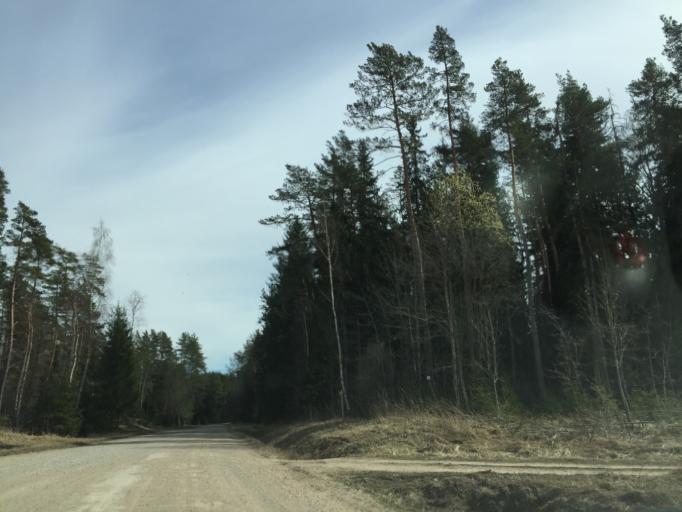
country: LV
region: Valkas Rajons
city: Valka
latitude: 57.8176
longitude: 25.9135
